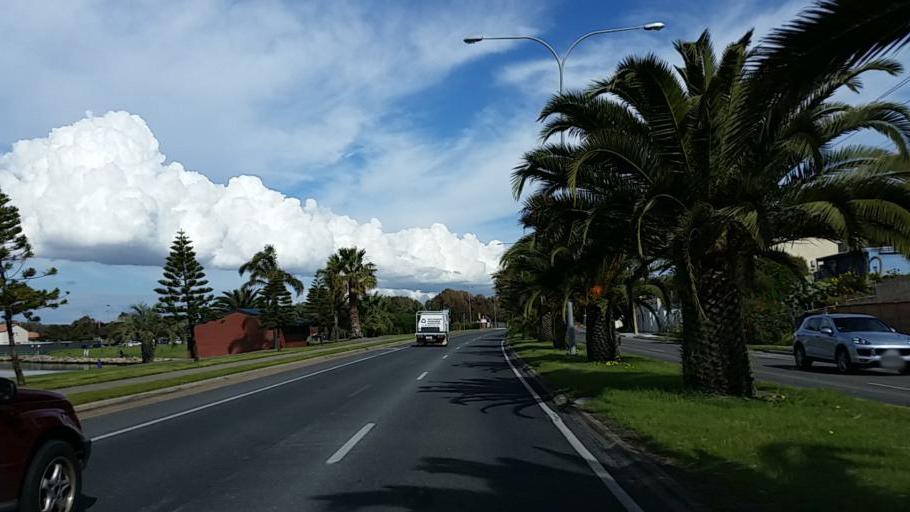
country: AU
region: South Australia
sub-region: Charles Sturt
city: Grange
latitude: -34.8926
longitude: 138.4883
